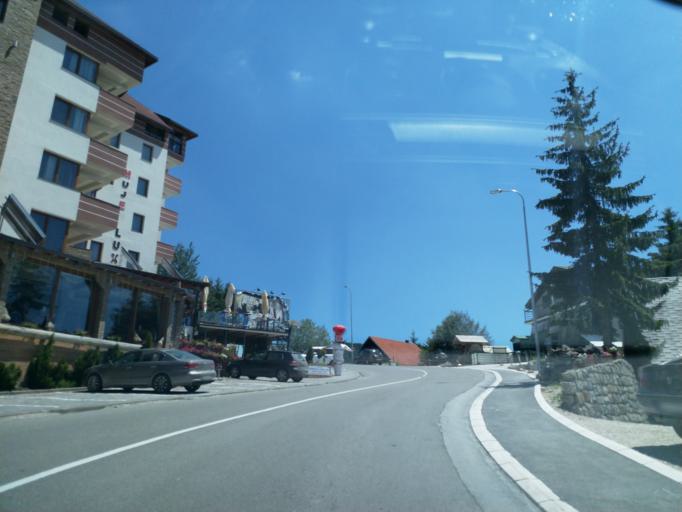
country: RS
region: Central Serbia
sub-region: Raski Okrug
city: Raska
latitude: 43.2737
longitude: 20.7823
